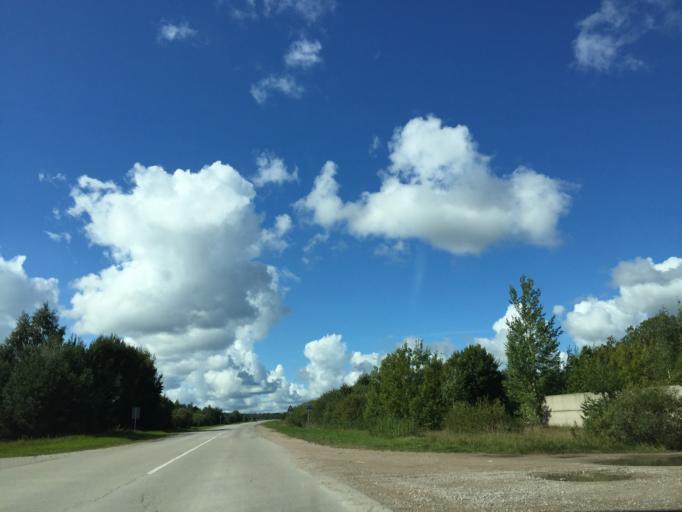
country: LV
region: Kuldigas Rajons
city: Kuldiga
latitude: 56.9655
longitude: 21.9188
